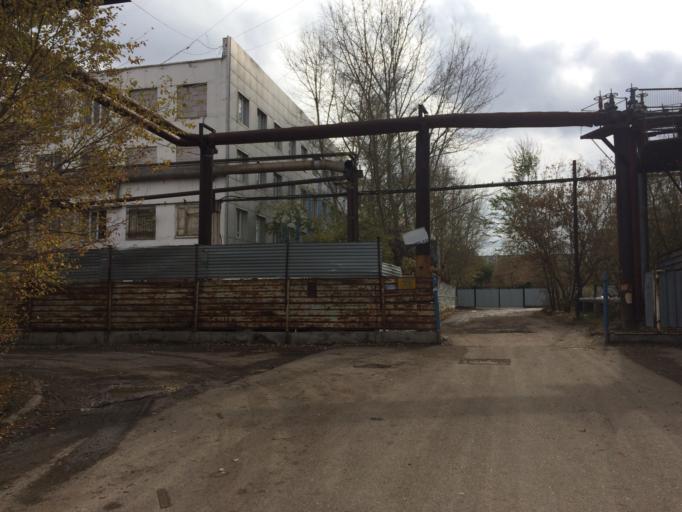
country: KZ
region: Astana Qalasy
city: Astana
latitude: 51.1826
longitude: 71.4318
